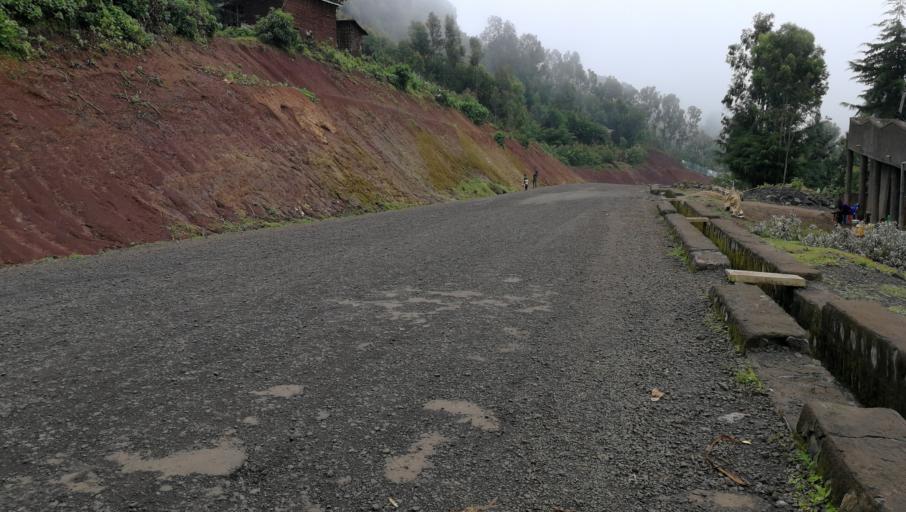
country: ET
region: Southern Nations, Nationalities, and People's Region
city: Areka
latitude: 7.0164
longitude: 37.2766
